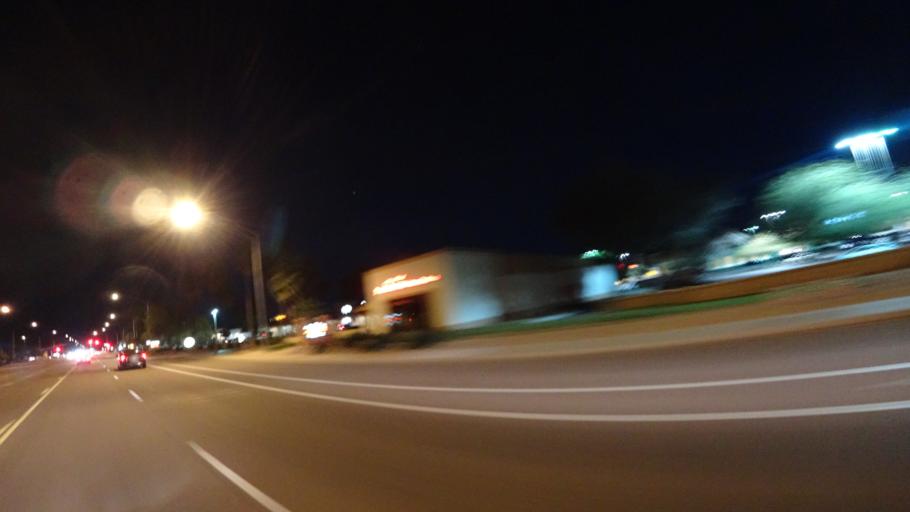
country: US
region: Arizona
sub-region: Maricopa County
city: Mesa
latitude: 33.4518
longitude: -111.7043
